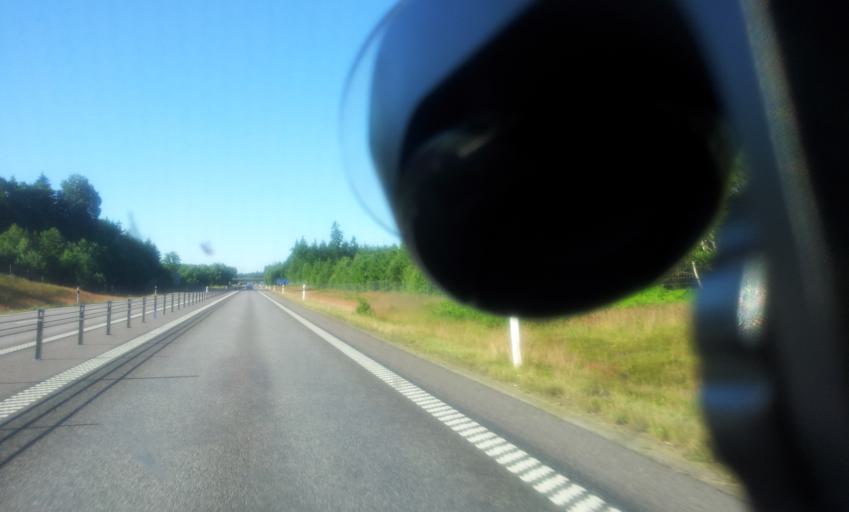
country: SE
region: Kalmar
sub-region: Kalmar Kommun
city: Ljungbyholm
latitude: 56.5578
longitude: 16.0870
